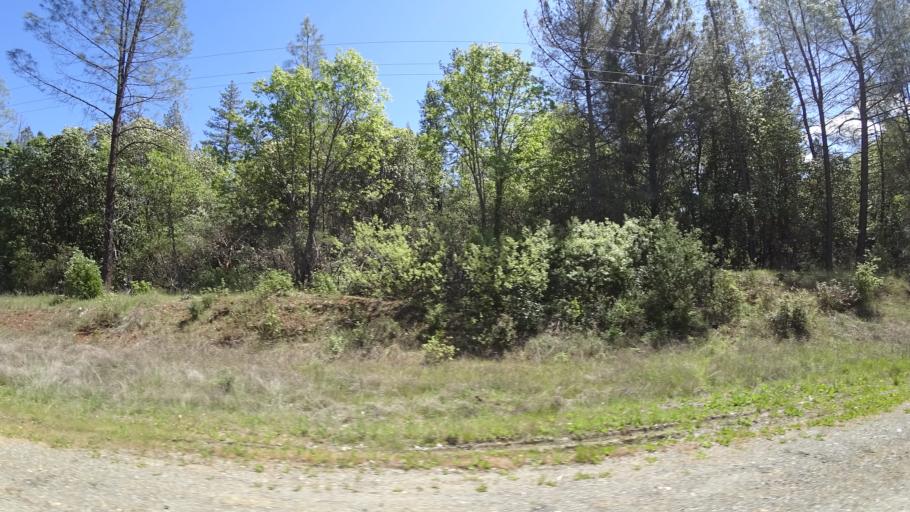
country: US
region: California
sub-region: Trinity County
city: Weaverville
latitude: 40.7260
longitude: -123.0459
